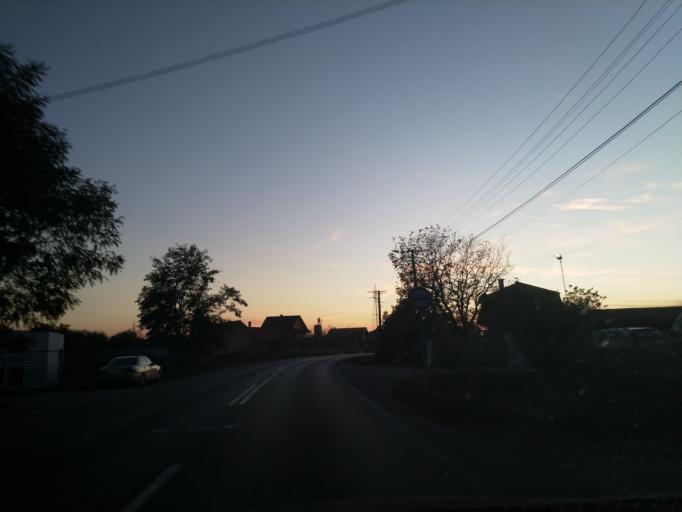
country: RS
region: Central Serbia
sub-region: Pomoravski Okrug
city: Svilajnac
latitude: 44.2308
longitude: 21.1816
